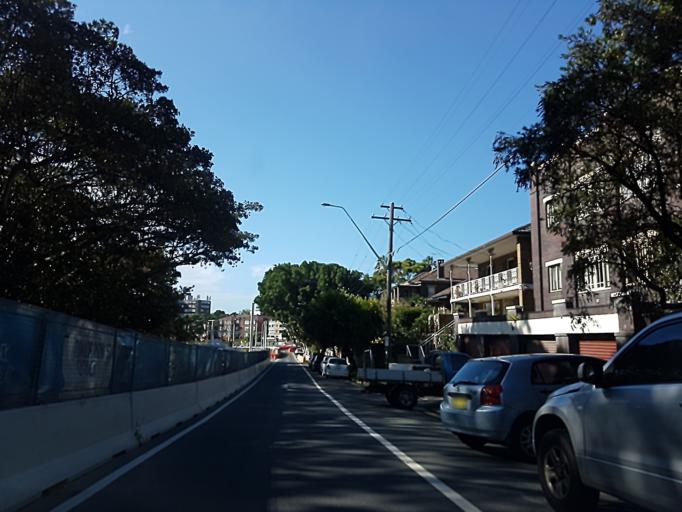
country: AU
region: New South Wales
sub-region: Randwick
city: Kingsford
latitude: -33.9131
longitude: 151.2354
